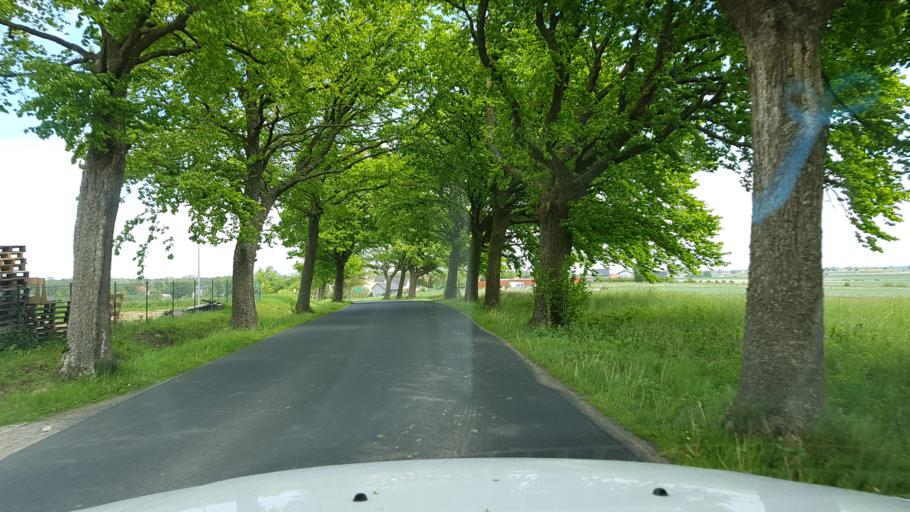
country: PL
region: West Pomeranian Voivodeship
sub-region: Powiat koszalinski
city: Mielno
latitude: 54.2450
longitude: 16.0039
